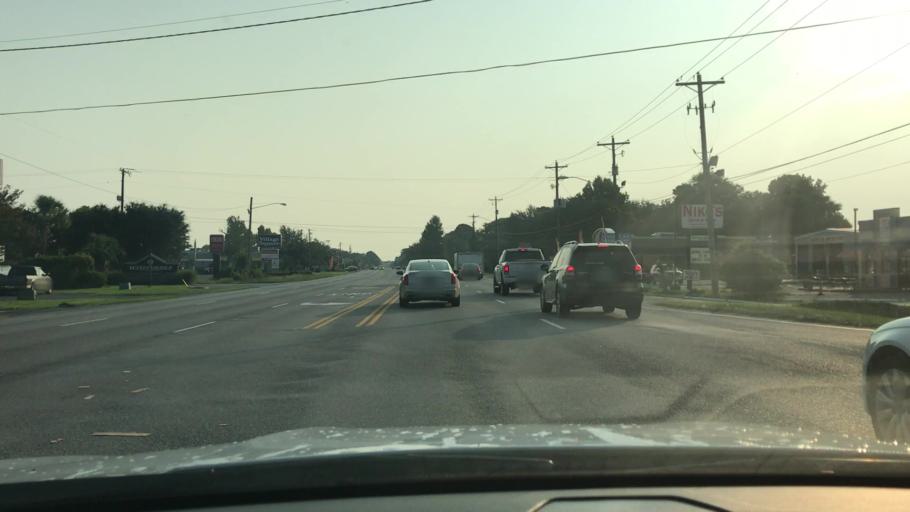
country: US
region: South Carolina
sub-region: Charleston County
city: North Charleston
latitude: 32.8032
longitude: -80.0149
